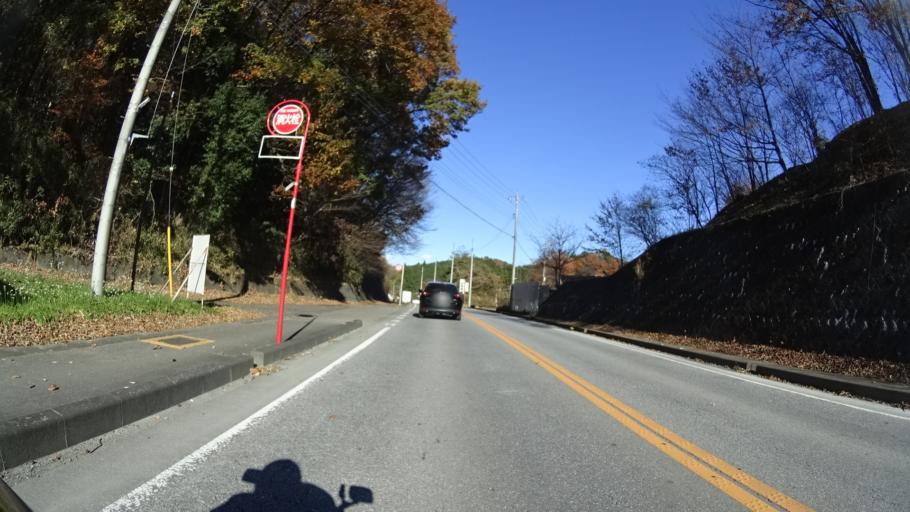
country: JP
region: Tochigi
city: Utsunomiya-shi
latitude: 36.5993
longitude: 139.8135
